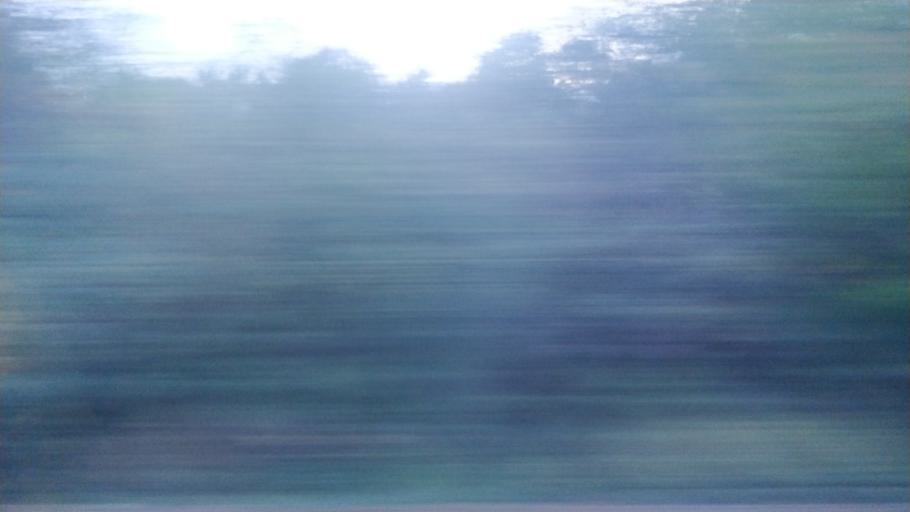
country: GB
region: England
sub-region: Borough of Wigan
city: Shevington
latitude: 53.5647
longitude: -2.7059
